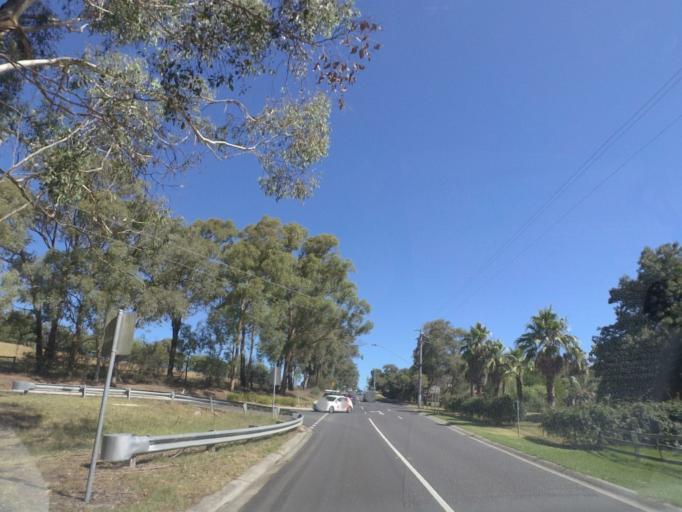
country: AU
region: Victoria
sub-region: Yarra Ranges
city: Chirnside Park
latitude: -37.7323
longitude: 145.2833
